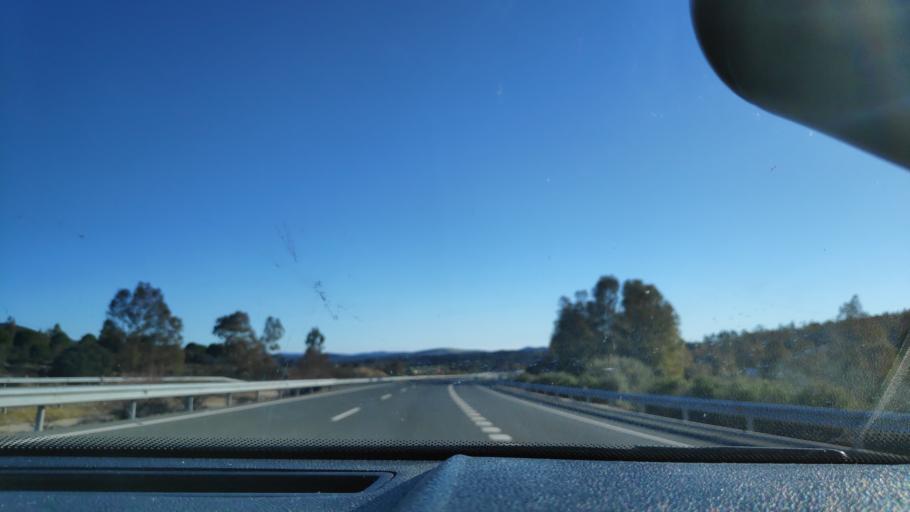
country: ES
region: Extremadura
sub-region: Provincia de Badajoz
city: Monesterio
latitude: 38.0349
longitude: -6.2237
